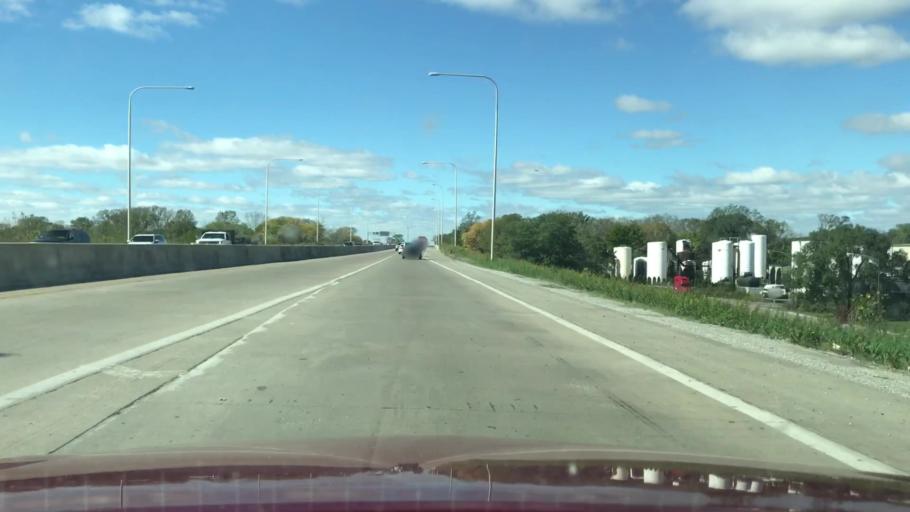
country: US
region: Illinois
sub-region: Cook County
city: Dolton
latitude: 41.7132
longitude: -87.5898
